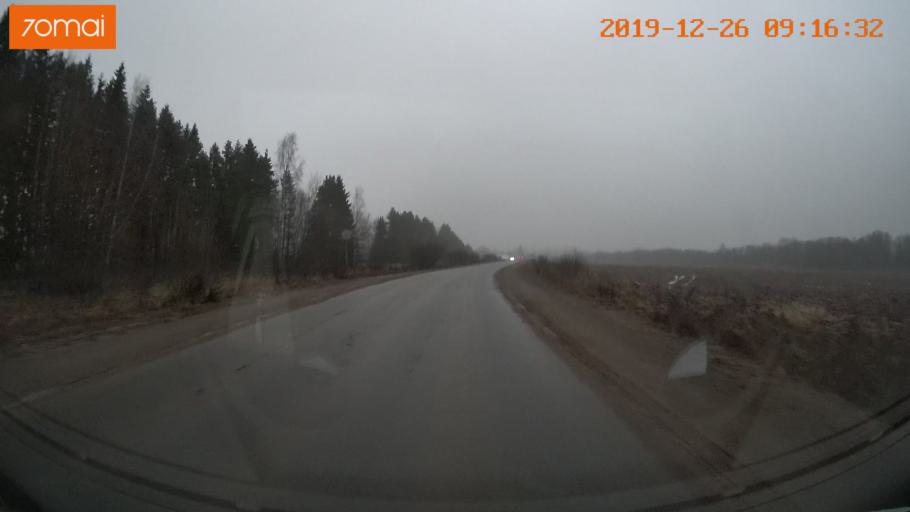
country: RU
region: Vologda
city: Gryazovets
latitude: 58.9197
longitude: 40.2389
